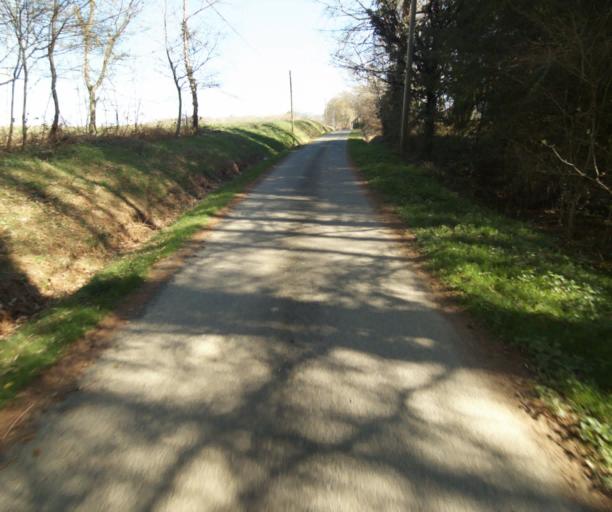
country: FR
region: Limousin
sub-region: Departement de la Correze
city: Seilhac
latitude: 45.4001
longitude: 1.7340
